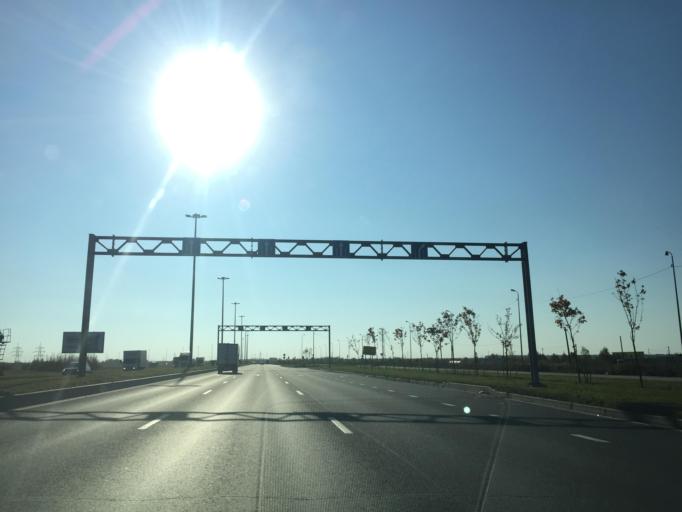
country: RU
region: St.-Petersburg
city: Petro-Slavyanka
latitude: 59.7725
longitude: 30.4996
